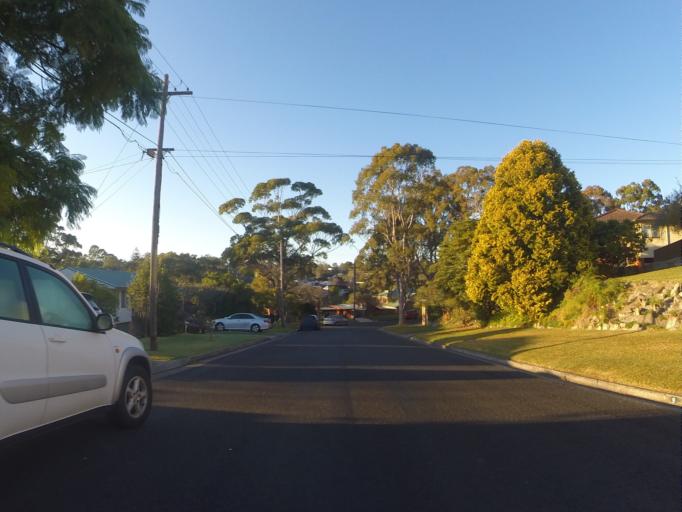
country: AU
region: New South Wales
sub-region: Sutherland Shire
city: Engadine
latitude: -34.0535
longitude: 151.0087
